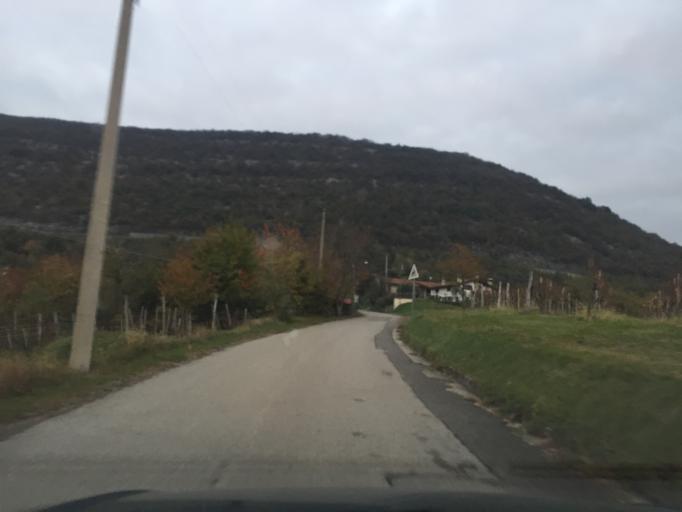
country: SI
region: Nova Gorica
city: Solkan
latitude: 45.9766
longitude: 13.6315
